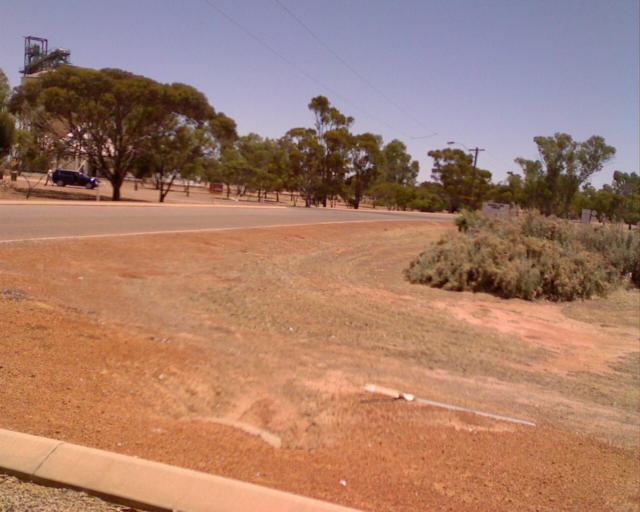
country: AU
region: Western Australia
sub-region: Wongan-Ballidu
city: Wongan Hills
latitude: -30.8295
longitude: 117.4808
